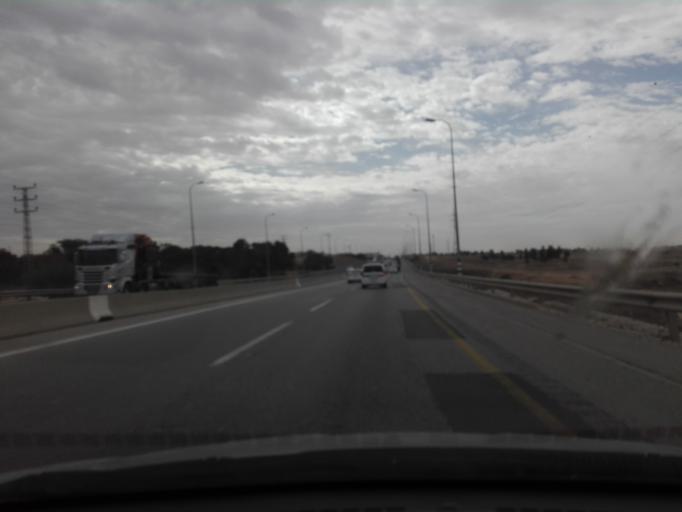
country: IL
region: Southern District
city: Lehavim
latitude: 31.3601
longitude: 34.7956
